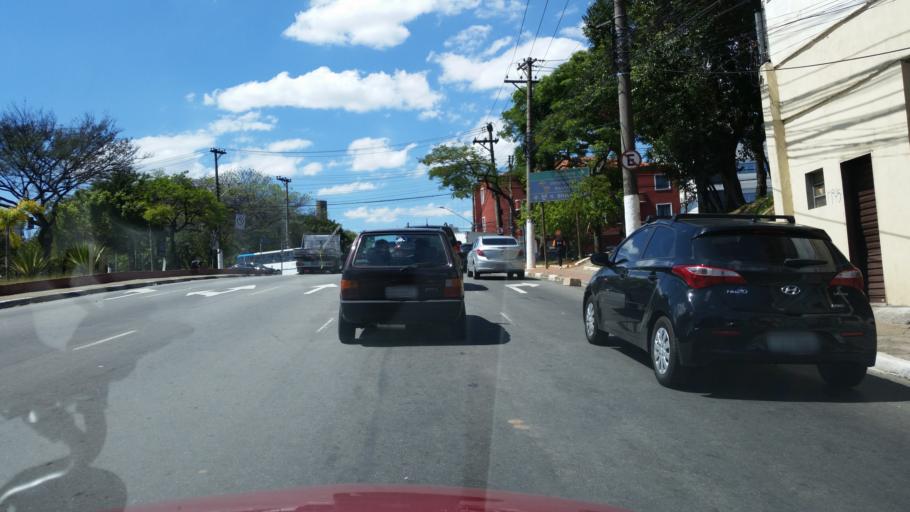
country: BR
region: Sao Paulo
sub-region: Diadema
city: Diadema
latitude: -23.6324
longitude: -46.6469
